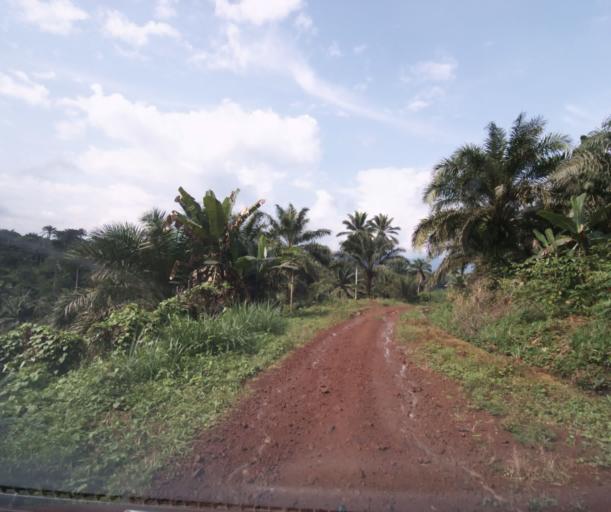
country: CM
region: Littoral
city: Melong
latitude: 5.0606
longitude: 9.9728
